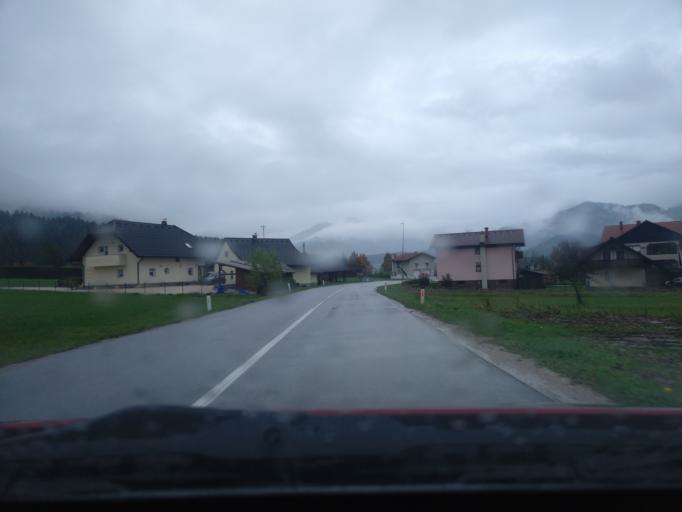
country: SI
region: Ljubno
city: Ljubno ob Savinji
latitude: 46.3255
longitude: 14.8484
